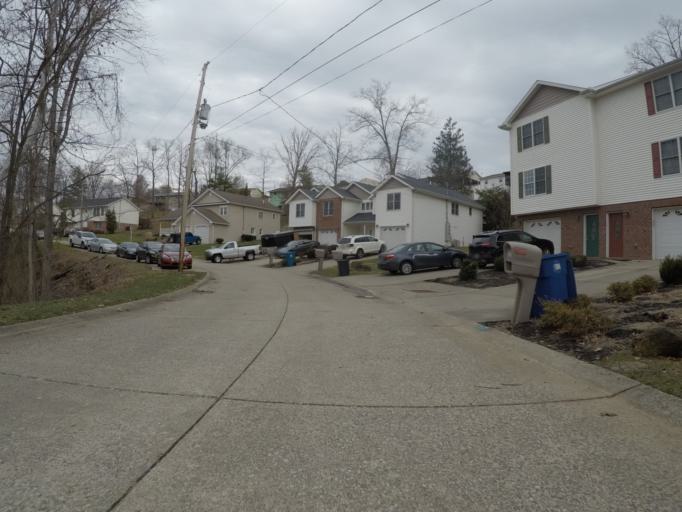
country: US
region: West Virginia
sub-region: Cabell County
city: Pea Ridge
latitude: 38.3929
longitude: -82.3790
